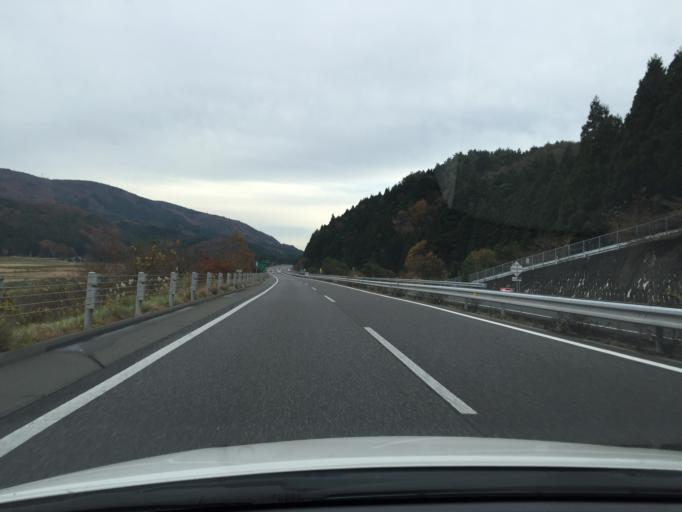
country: JP
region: Fukushima
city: Iwaki
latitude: 37.1098
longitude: 140.7574
